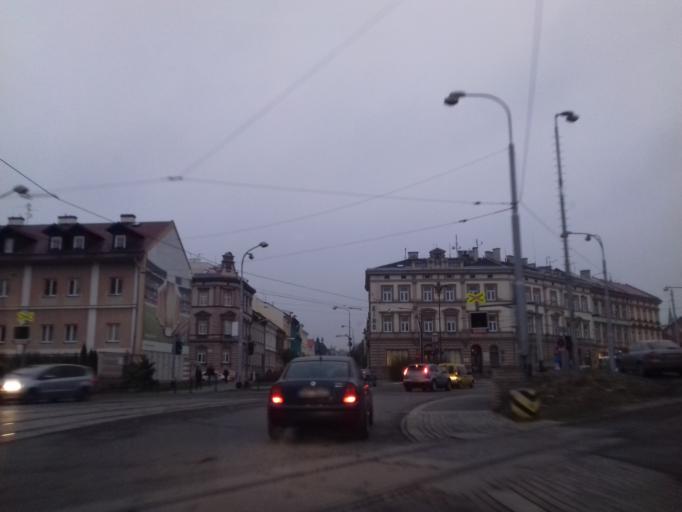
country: CZ
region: Olomoucky
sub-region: Okres Olomouc
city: Olomouc
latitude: 49.5952
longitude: 17.2415
